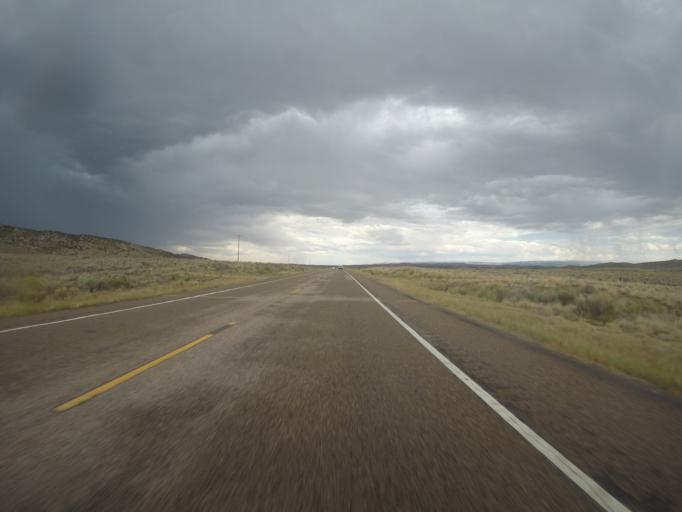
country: US
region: Colorado
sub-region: Rio Blanco County
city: Rangely
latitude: 40.2400
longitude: -108.9255
